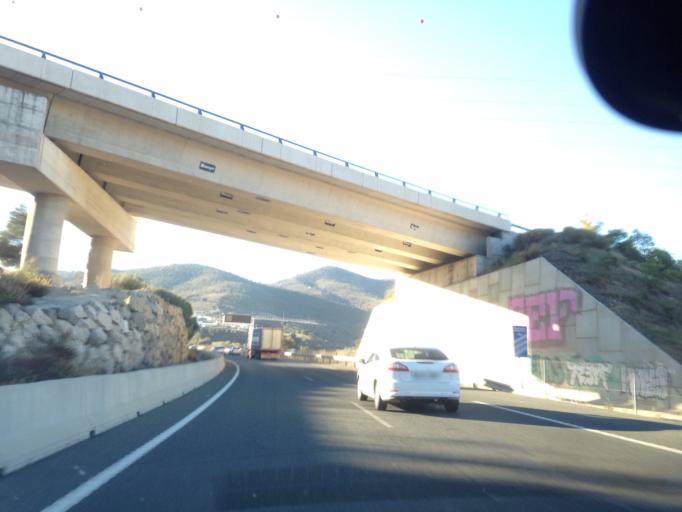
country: ES
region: Andalusia
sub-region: Provincia de Malaga
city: Casabermeja
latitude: 36.9083
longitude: -4.4464
